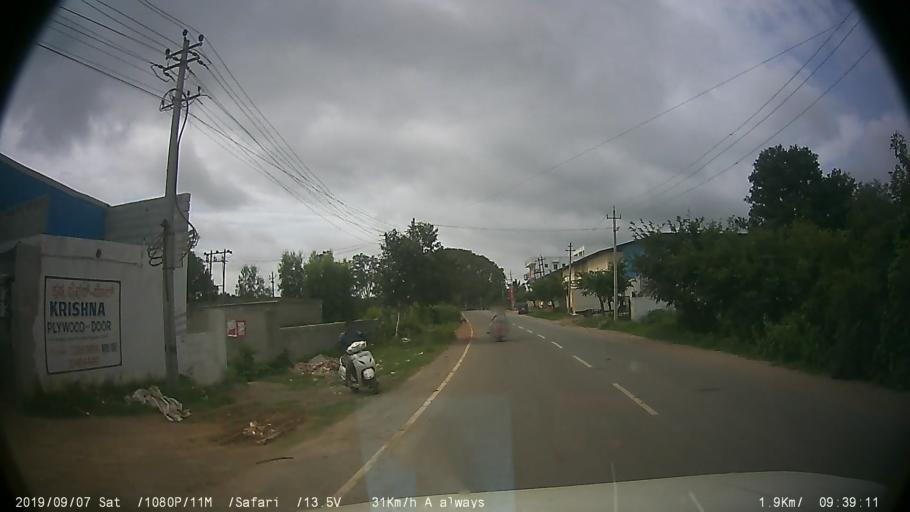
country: IN
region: Karnataka
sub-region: Bangalore Urban
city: Anekal
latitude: 12.8149
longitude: 77.6277
